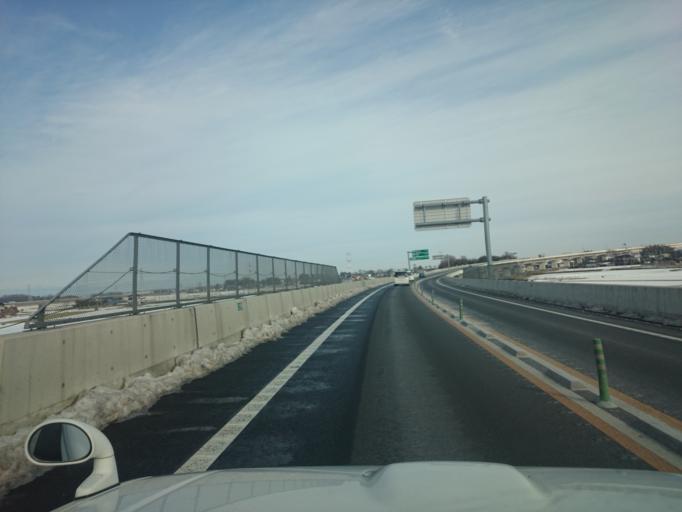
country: JP
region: Ibaraki
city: Sakai
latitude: 36.1058
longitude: 139.7565
